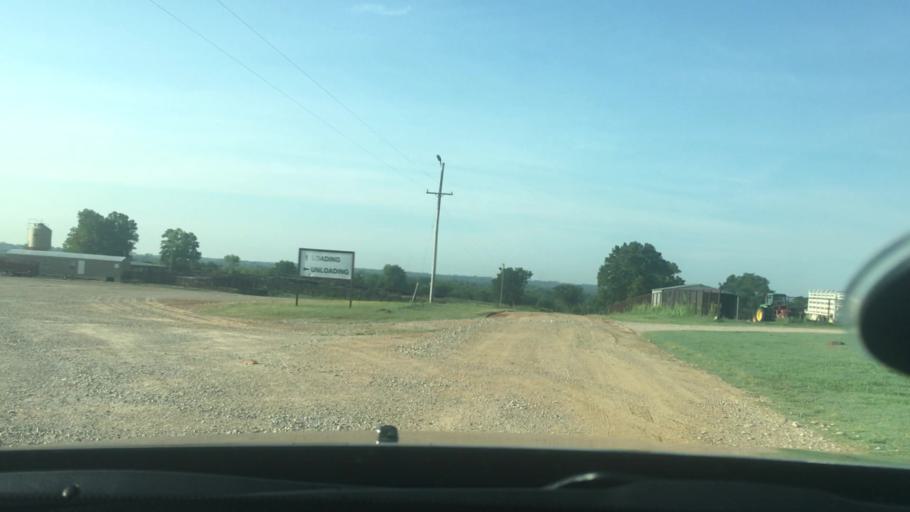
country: US
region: Oklahoma
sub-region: Pontotoc County
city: Ada
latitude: 34.7816
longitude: -96.7221
